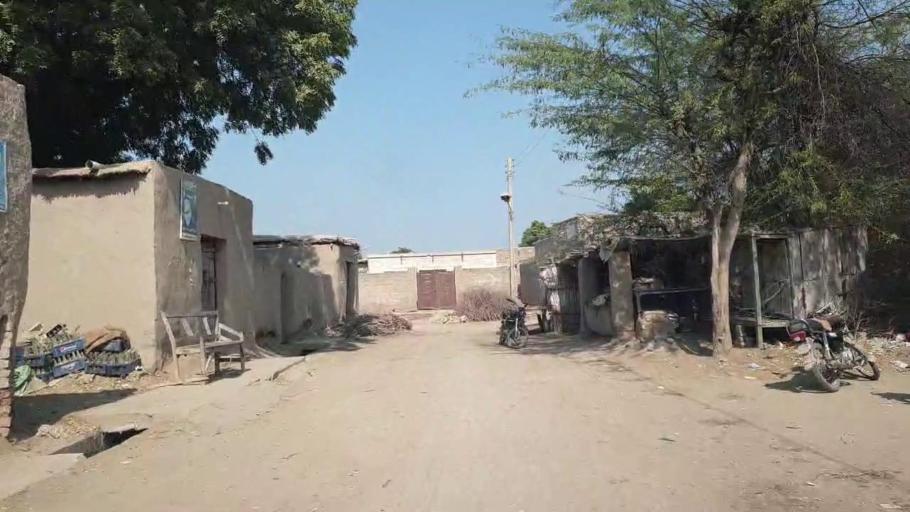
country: PK
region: Sindh
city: Chambar
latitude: 25.4134
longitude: 68.8969
